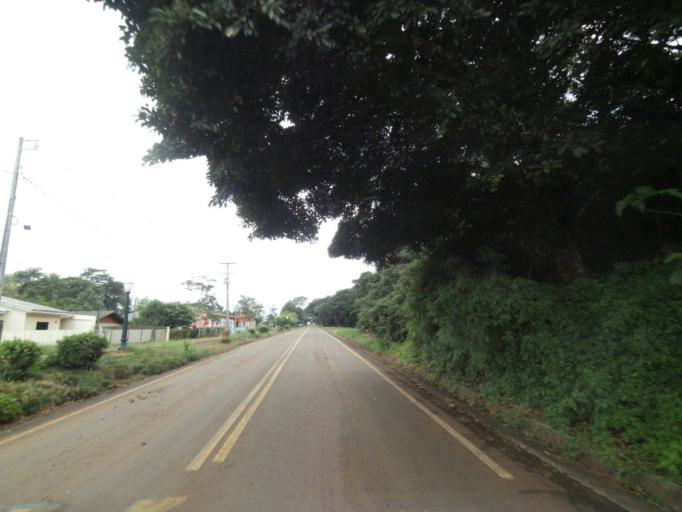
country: BR
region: Parana
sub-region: Guaraniacu
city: Guaraniacu
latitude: -25.0966
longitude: -52.8815
